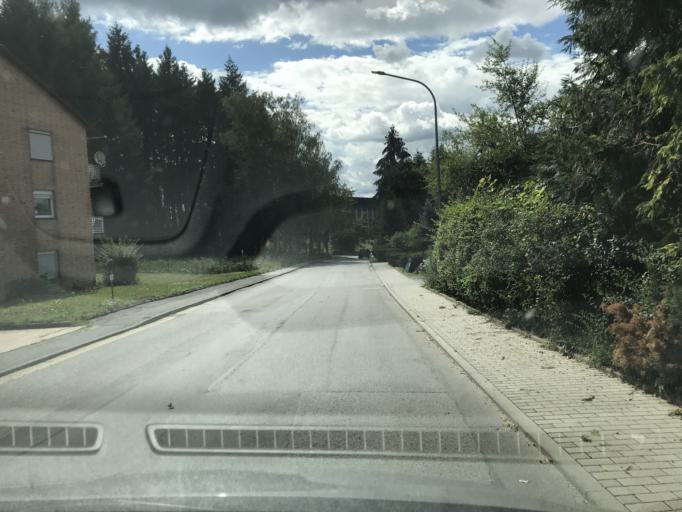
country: DE
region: Hesse
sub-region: Regierungsbezirk Darmstadt
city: Lindenfels
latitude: 49.6657
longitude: 8.7450
